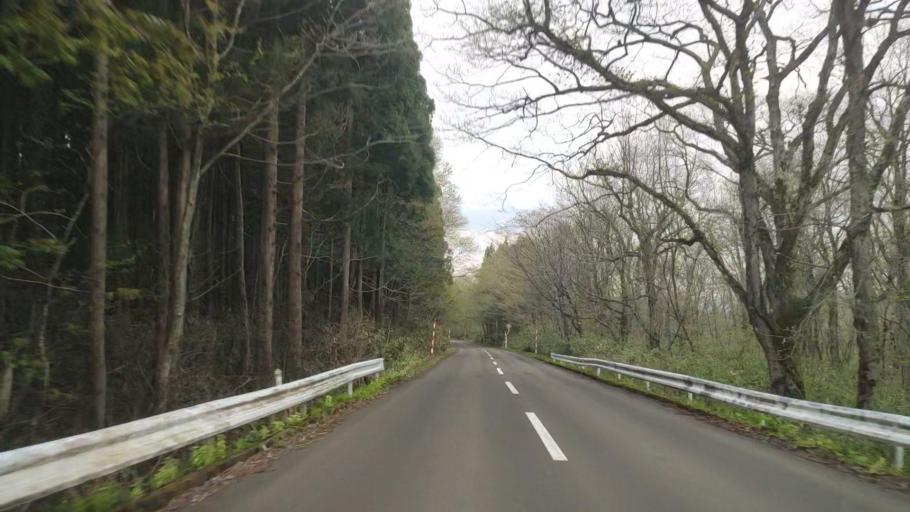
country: JP
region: Akita
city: Hanawa
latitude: 40.3949
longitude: 140.7964
